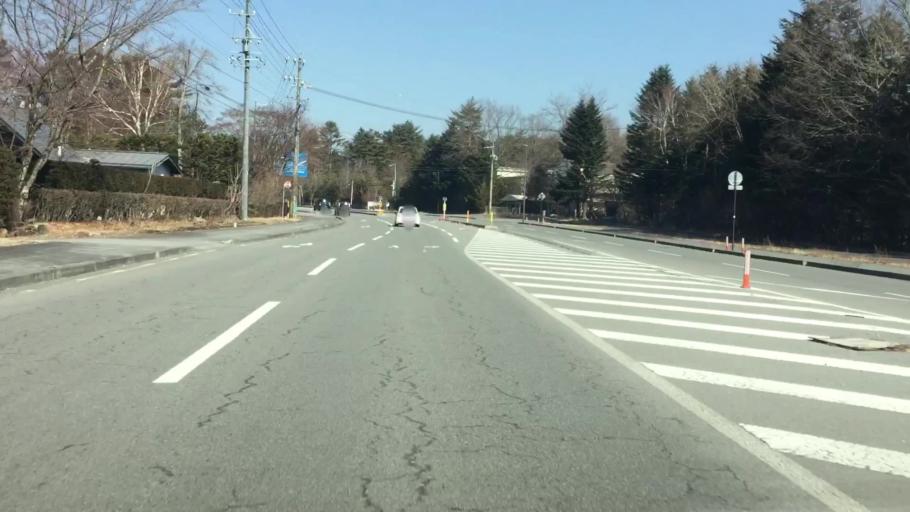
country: JP
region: Nagano
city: Saku
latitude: 36.3189
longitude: 138.6309
